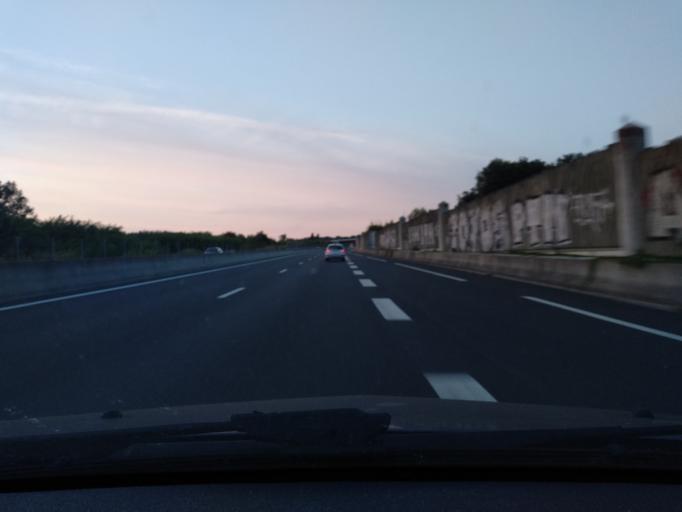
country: FR
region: Centre
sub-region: Departement d'Indre-et-Loire
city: La Membrolle-sur-Choisille
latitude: 47.4210
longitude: 0.6353
